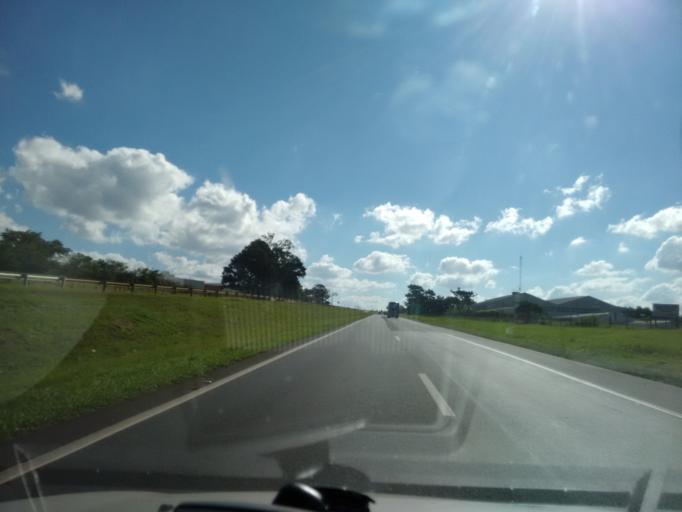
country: BR
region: Sao Paulo
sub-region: Sao Carlos
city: Sao Carlos
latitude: -21.9791
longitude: -47.9237
